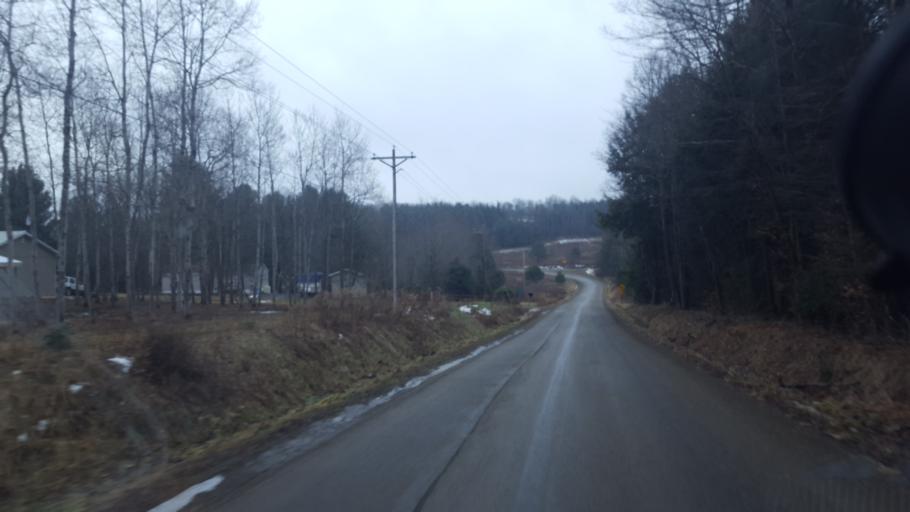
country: US
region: New York
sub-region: Allegany County
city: Andover
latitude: 41.9806
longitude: -77.7452
